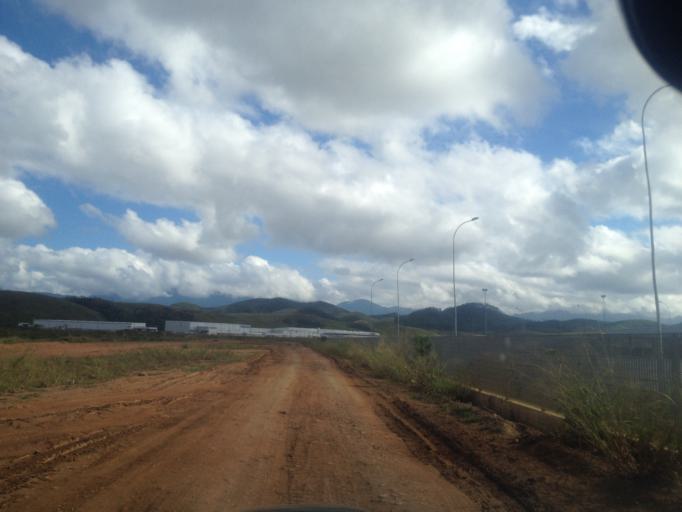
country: BR
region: Rio de Janeiro
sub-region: Resende
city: Resende
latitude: -22.4378
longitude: -44.3852
